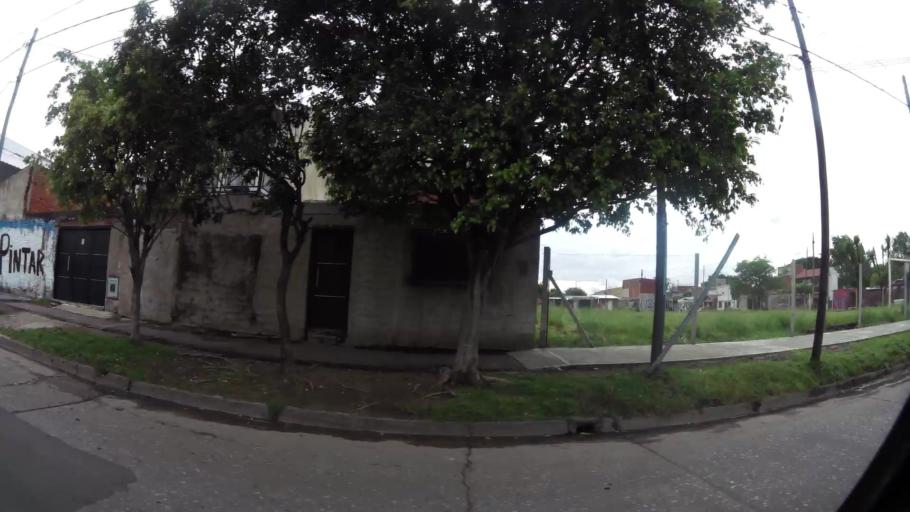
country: AR
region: Buenos Aires
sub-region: Partido de Lanus
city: Lanus
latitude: -34.7238
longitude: -58.3681
